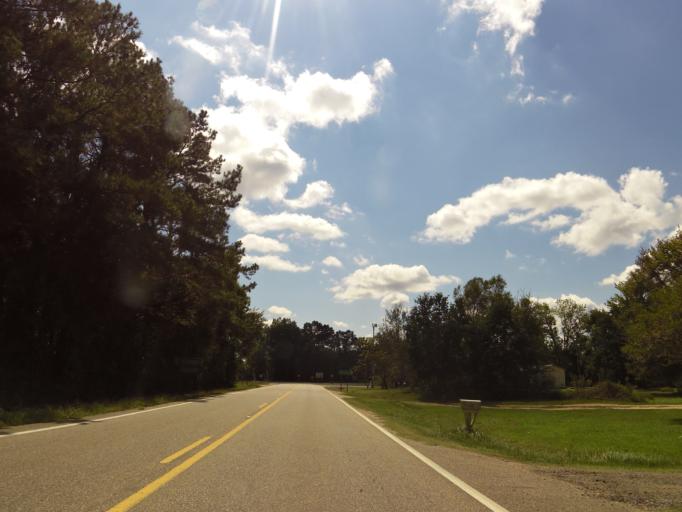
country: US
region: Alabama
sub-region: Dallas County
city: Selma
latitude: 32.4664
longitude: -87.0926
